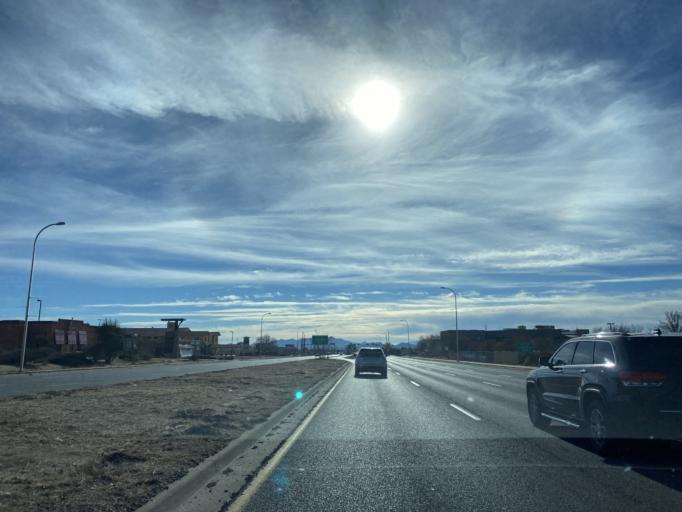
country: US
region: New Mexico
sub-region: Santa Fe County
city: Agua Fria
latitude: 35.6373
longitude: -106.0185
